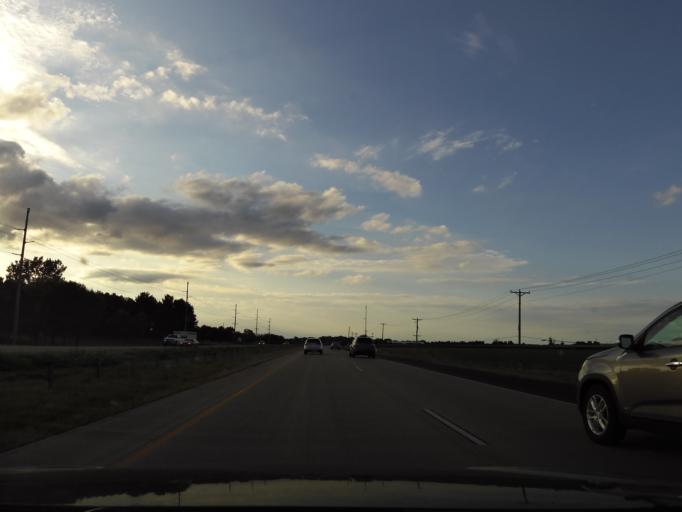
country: US
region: Minnesota
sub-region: Dakota County
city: Hastings
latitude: 44.7874
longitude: -92.8802
